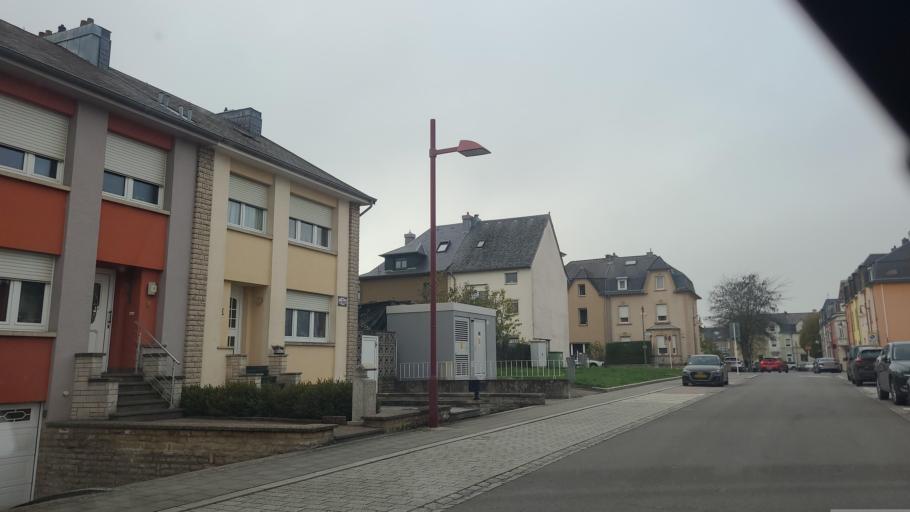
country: LU
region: Luxembourg
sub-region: Canton d'Esch-sur-Alzette
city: Petange
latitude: 49.5586
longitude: 5.8825
